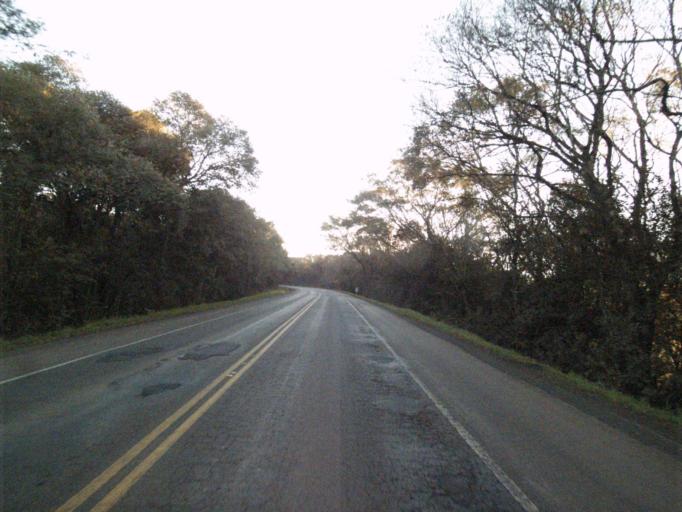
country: BR
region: Santa Catarina
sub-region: Sao Lourenco Do Oeste
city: Sao Lourenco dOeste
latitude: -26.8289
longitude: -53.1128
